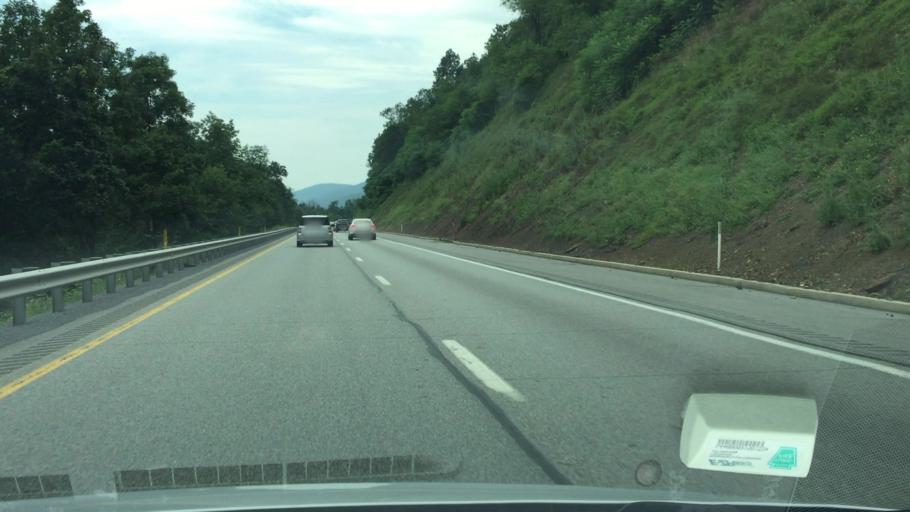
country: US
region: Pennsylvania
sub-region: Bedford County
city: Earlston
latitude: 39.8749
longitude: -78.2508
